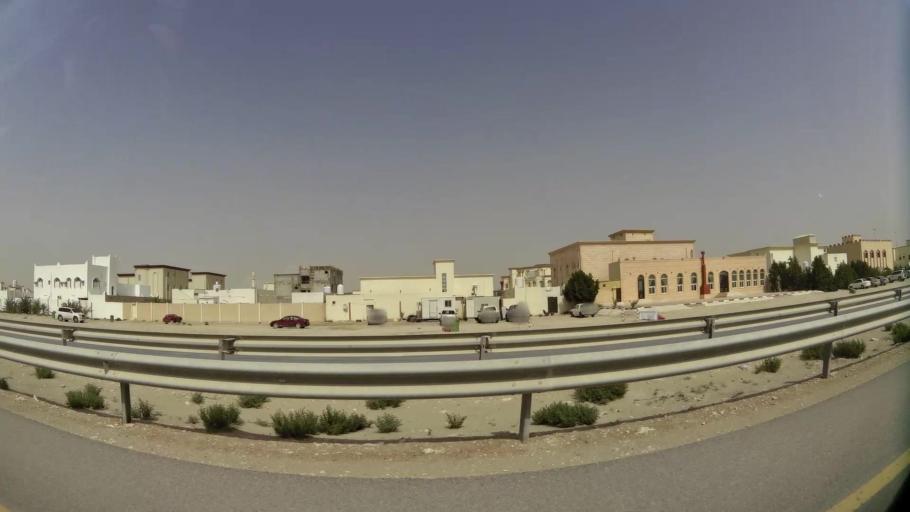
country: QA
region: Baladiyat ar Rayyan
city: Ar Rayyan
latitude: 25.1882
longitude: 51.3609
